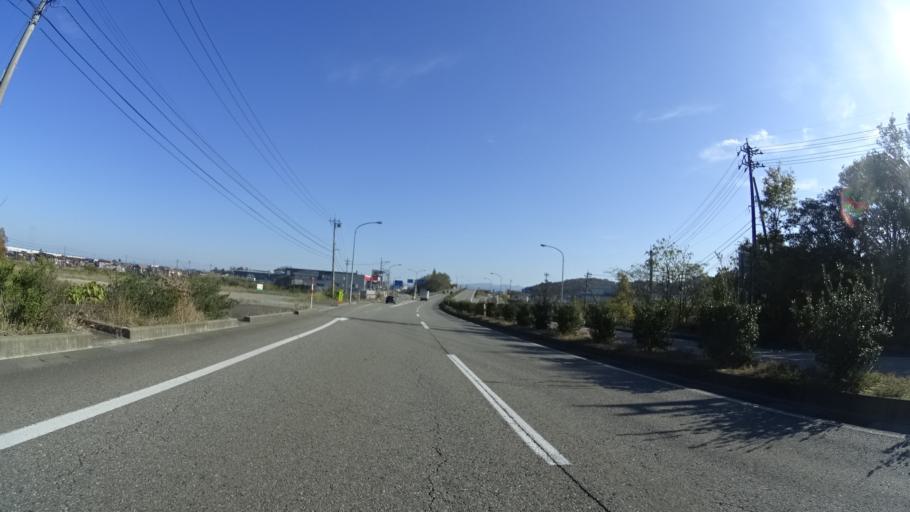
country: JP
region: Ishikawa
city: Komatsu
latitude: 36.3247
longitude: 136.4070
